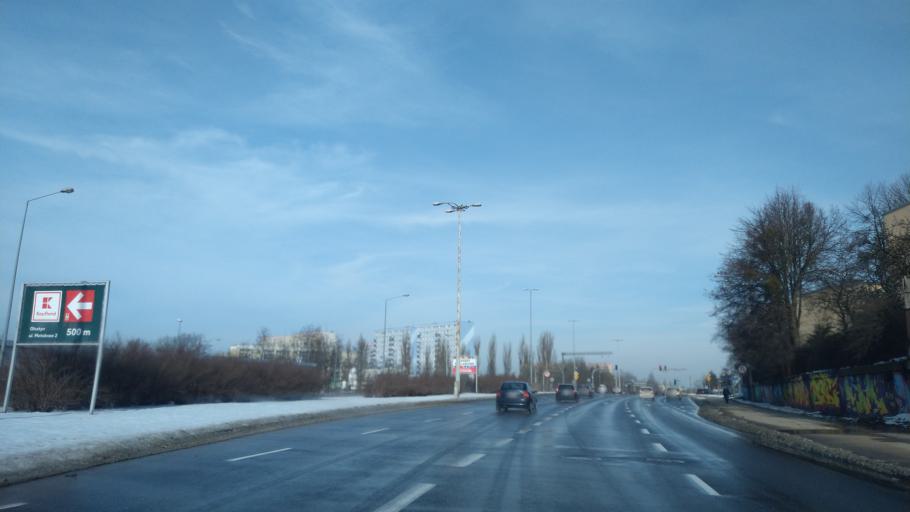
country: PL
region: Warmian-Masurian Voivodeship
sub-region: Powiat olsztynski
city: Olsztyn
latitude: 53.7615
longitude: 20.5001
